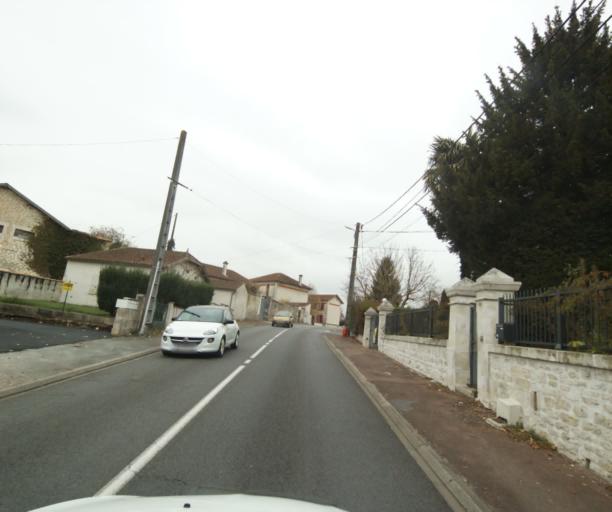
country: FR
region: Poitou-Charentes
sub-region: Departement de la Charente-Maritime
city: Saintes
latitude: 45.7544
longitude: -0.6318
